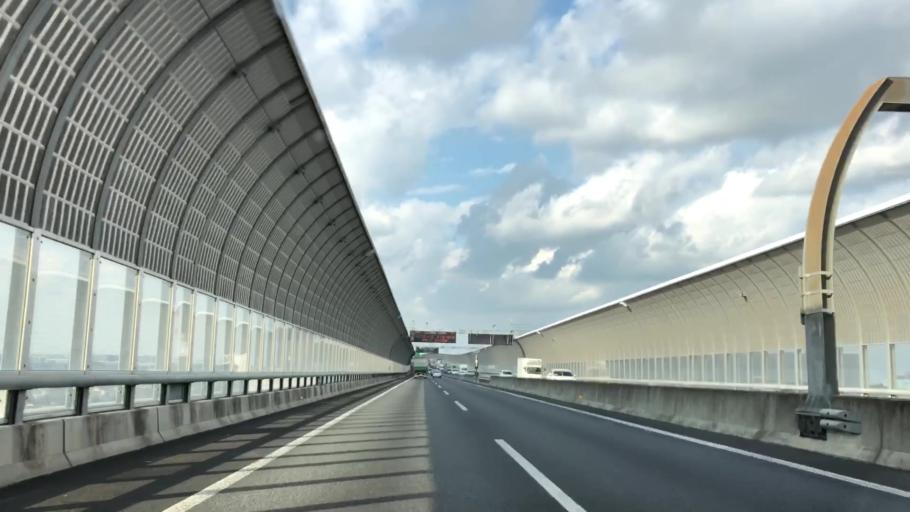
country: JP
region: Chiba
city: Matsudo
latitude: 35.8119
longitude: 139.8754
